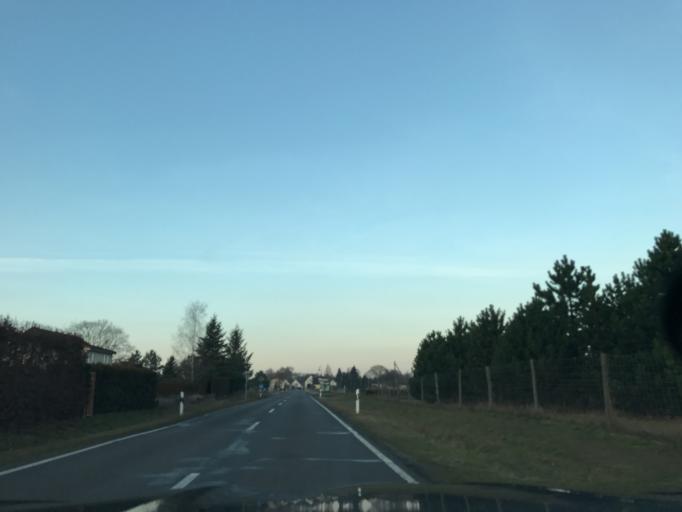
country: DE
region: Brandenburg
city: Wusterwitz
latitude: 52.4354
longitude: 12.4268
